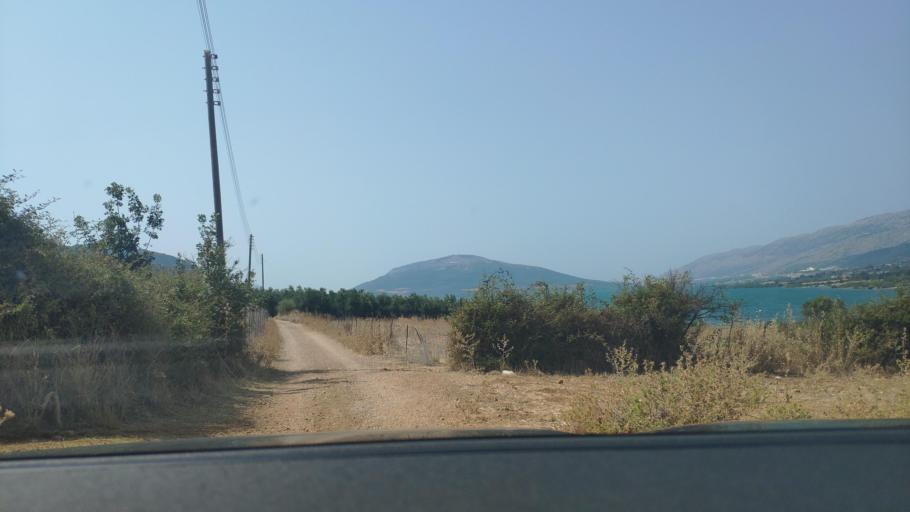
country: GR
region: West Greece
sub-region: Nomos Aitolias kai Akarnanias
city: Fitiai
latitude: 38.7212
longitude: 21.1941
